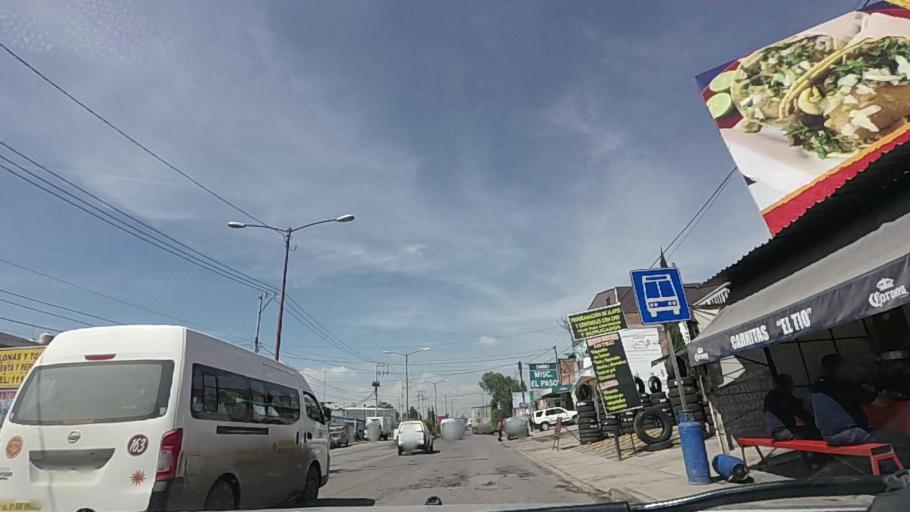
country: MX
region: Mexico
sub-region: Cuautitlan
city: San Jose del Puente
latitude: 19.7232
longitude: -99.1901
